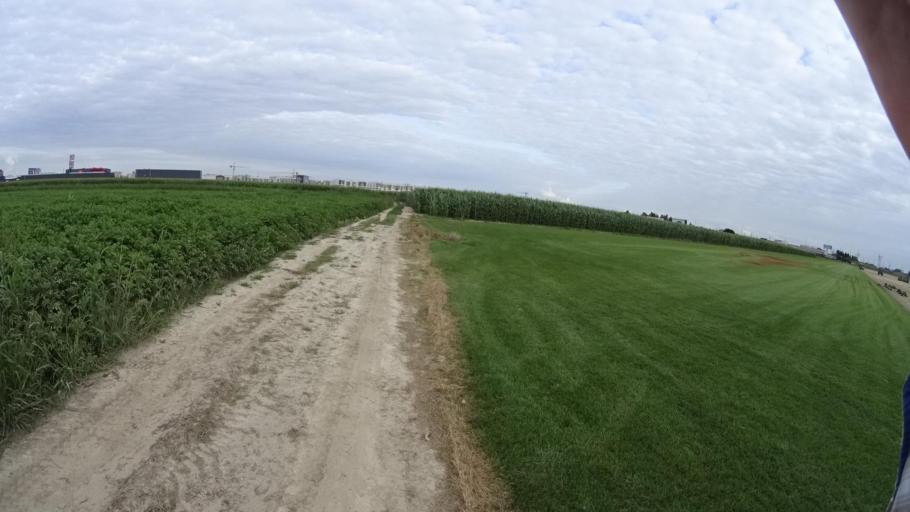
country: PL
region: Masovian Voivodeship
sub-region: Powiat warszawski zachodni
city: Babice
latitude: 52.2330
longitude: 20.8758
